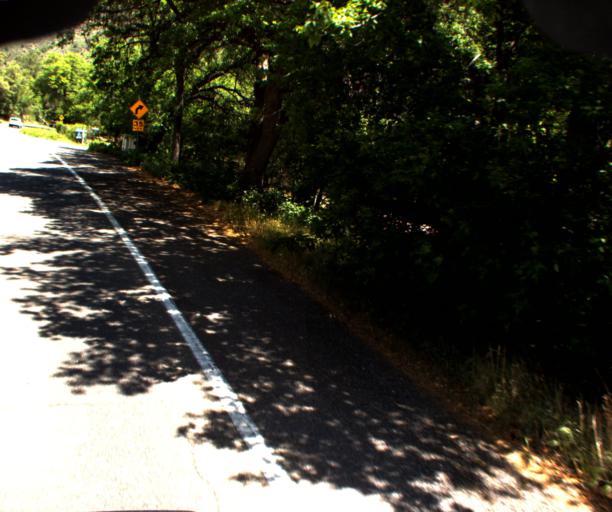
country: US
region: Arizona
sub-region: Coconino County
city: Sedona
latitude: 34.9116
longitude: -111.7282
